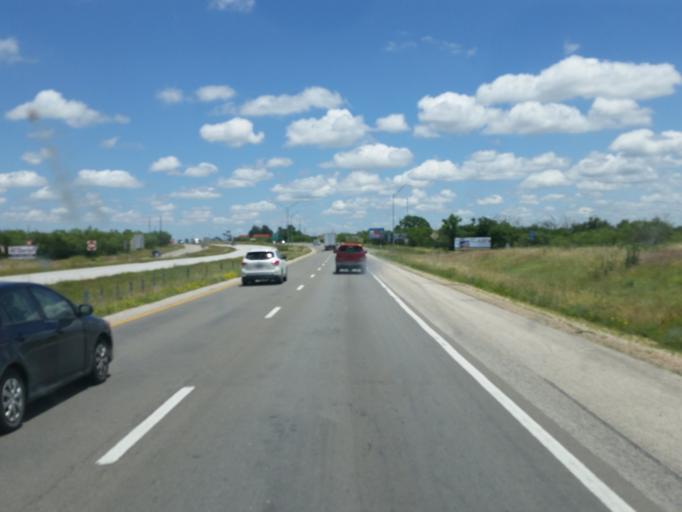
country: US
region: Texas
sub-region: Nolan County
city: Sweetwater
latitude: 32.4476
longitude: -100.4147
